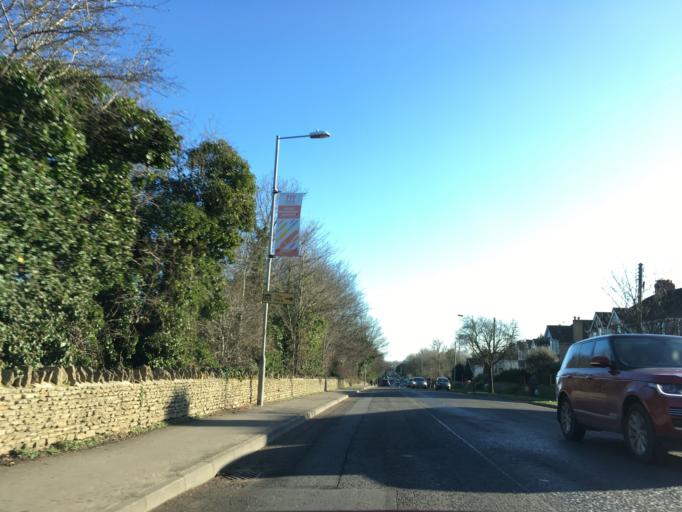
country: GB
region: England
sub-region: Wiltshire
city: Chippenham
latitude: 51.4650
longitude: -2.1325
